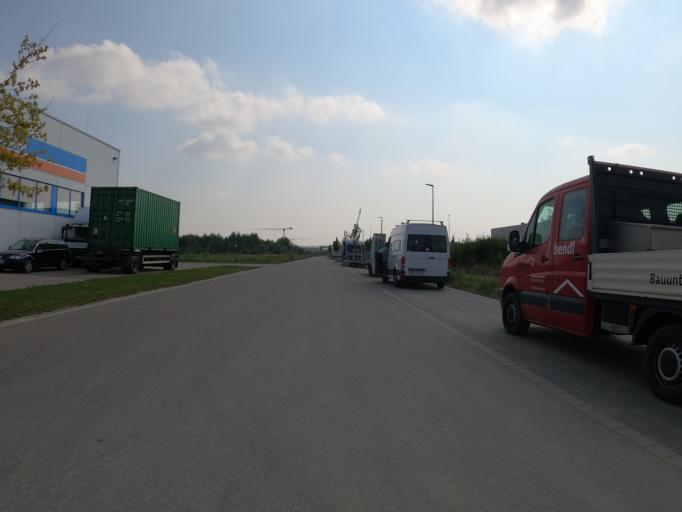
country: DE
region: Bavaria
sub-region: Swabia
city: Bubesheim
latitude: 48.4460
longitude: 10.2392
